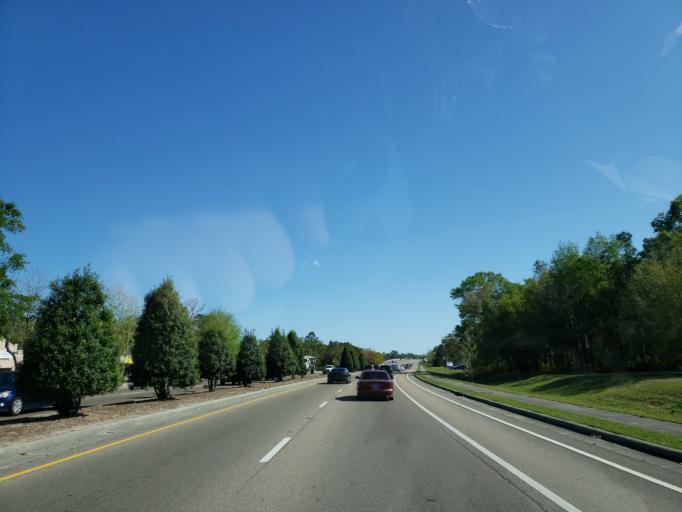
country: US
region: Mississippi
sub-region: Harrison County
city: West Gulfport
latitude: 30.4120
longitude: -89.0283
